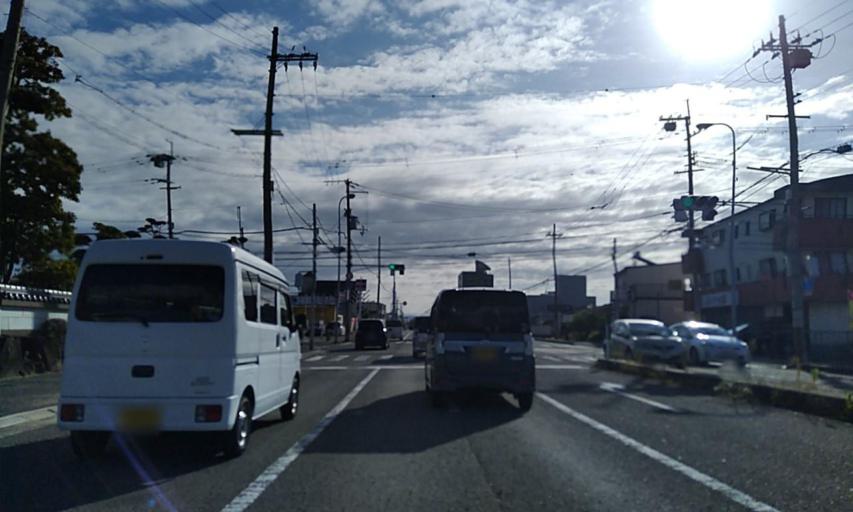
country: JP
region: Wakayama
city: Minato
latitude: 34.2587
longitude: 135.1150
